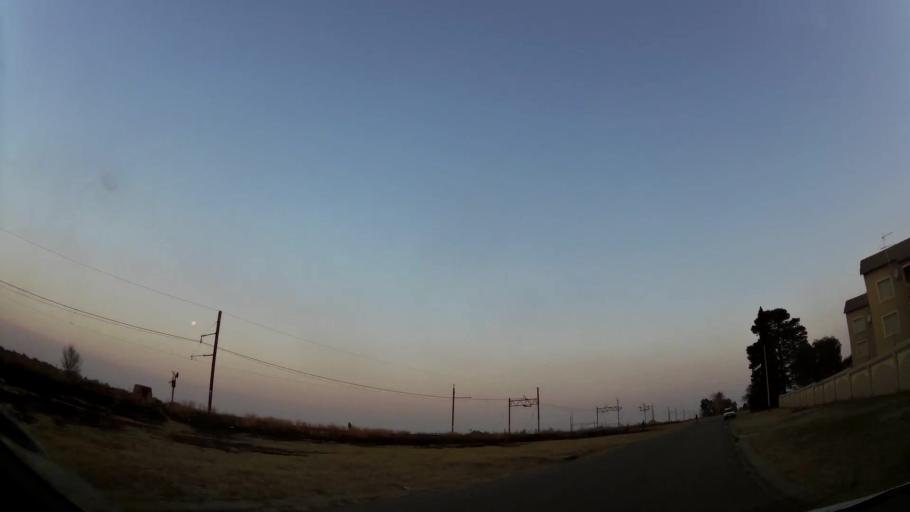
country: ZA
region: Gauteng
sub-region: Ekurhuleni Metropolitan Municipality
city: Nigel
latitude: -26.3447
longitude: 28.4407
